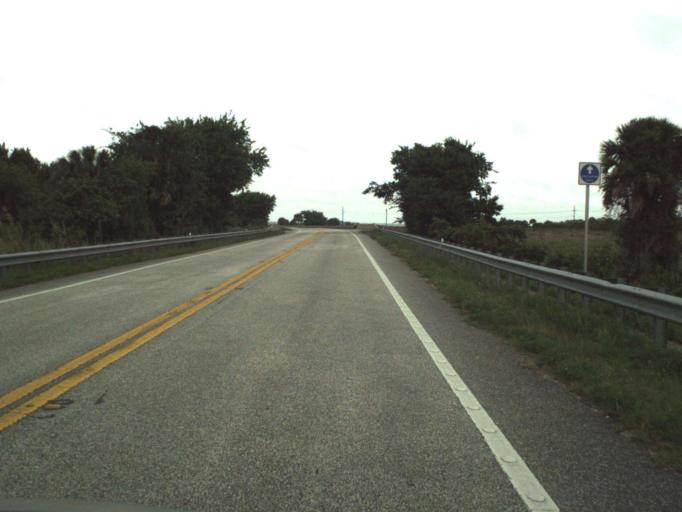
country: US
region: Florida
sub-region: Seminole County
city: Geneva
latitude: 28.7099
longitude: -81.0219
